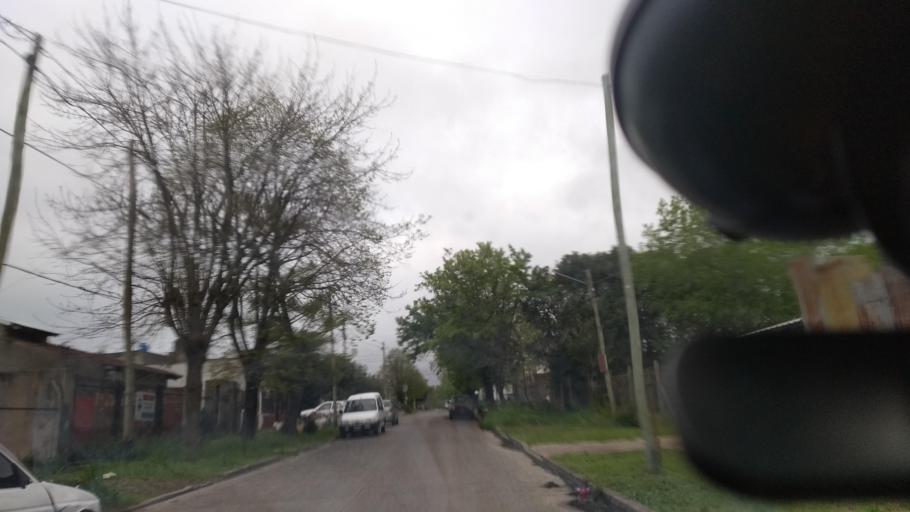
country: AR
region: Buenos Aires
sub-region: Partido de La Plata
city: La Plata
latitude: -34.9488
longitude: -57.9867
